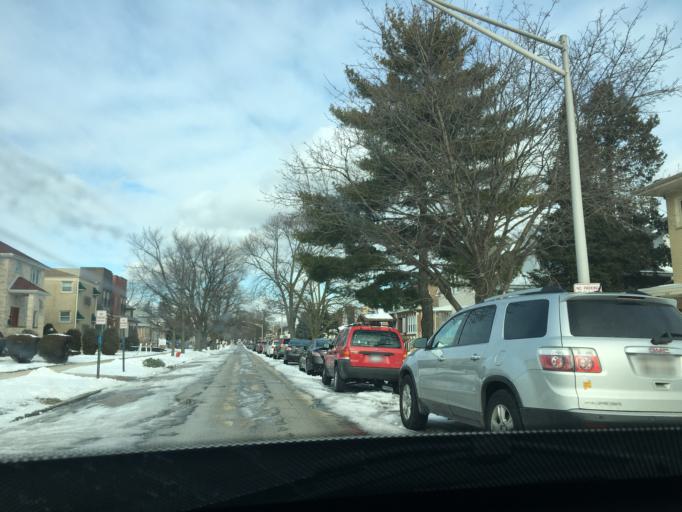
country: US
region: Illinois
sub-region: Cook County
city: Elmwood Park
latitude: 41.9276
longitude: -87.8125
